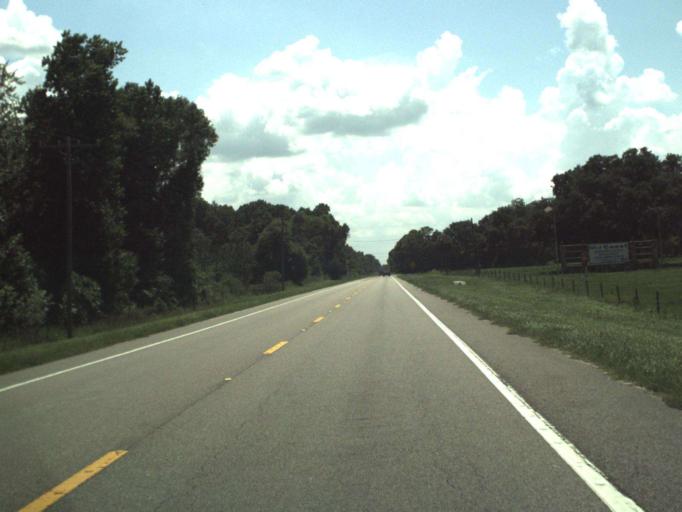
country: US
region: Florida
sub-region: Lake County
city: Mascotte
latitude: 28.5771
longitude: -81.9845
